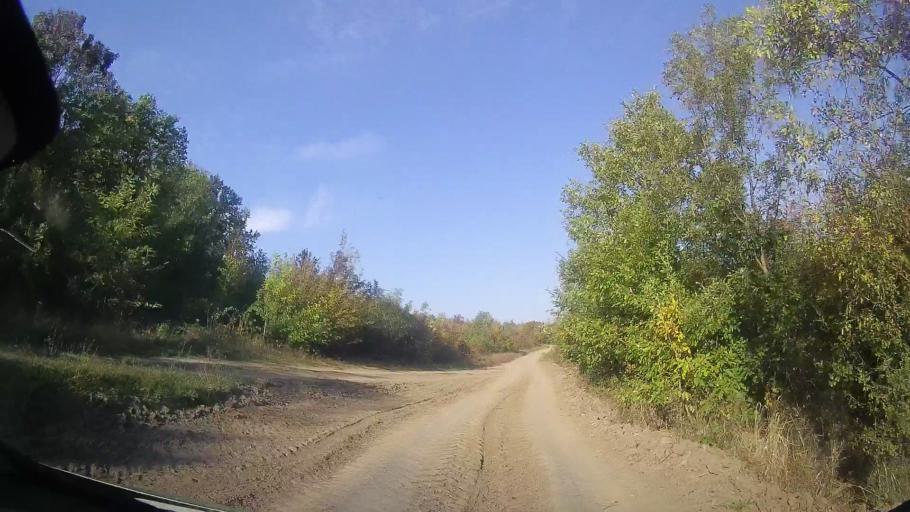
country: RO
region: Timis
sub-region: Comuna Bogda
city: Bogda
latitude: 45.9088
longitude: 21.5873
